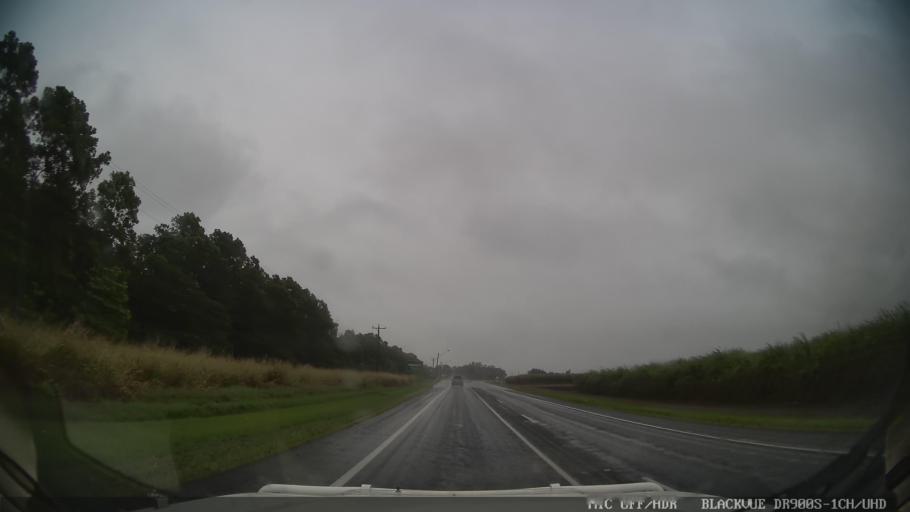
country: AU
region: Queensland
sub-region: Cassowary Coast
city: Innisfail
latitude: -17.7515
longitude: 146.0277
